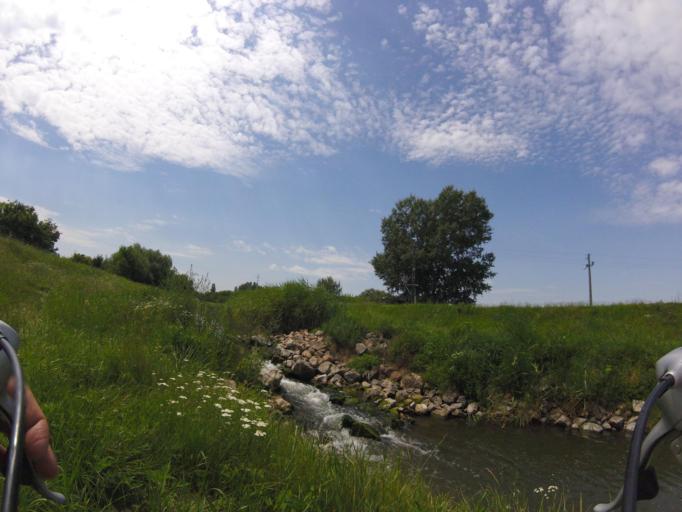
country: HU
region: Komarom-Esztergom
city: Dunaalmas
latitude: 47.7269
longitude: 18.3147
